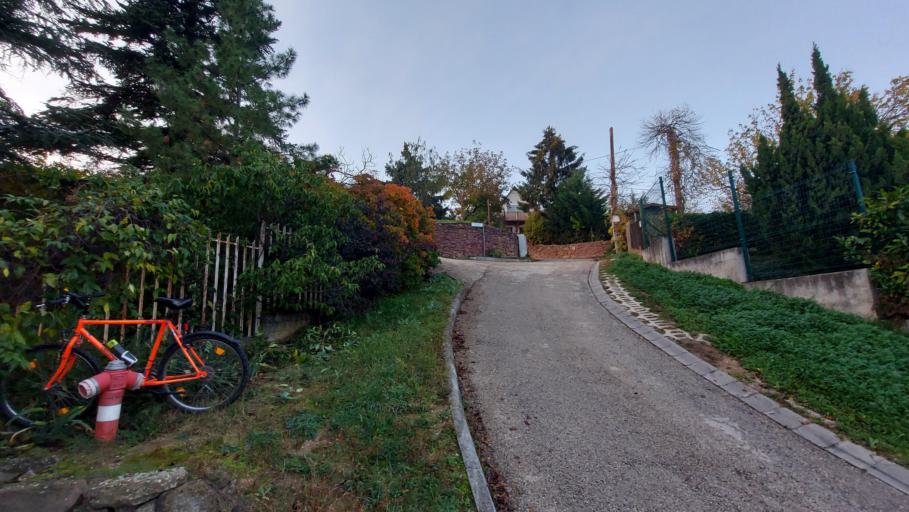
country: HU
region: Veszprem
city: Balatonalmadi
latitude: 47.0206
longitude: 17.9958
